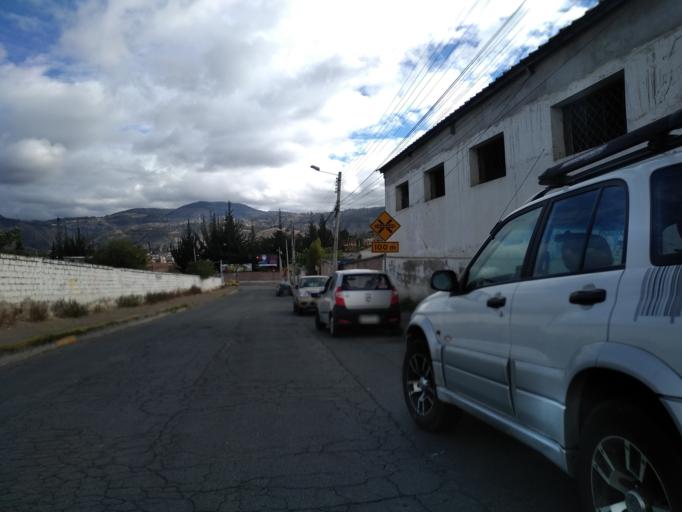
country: EC
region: Chimborazo
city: Riobamba
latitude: -1.6664
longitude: -78.6674
